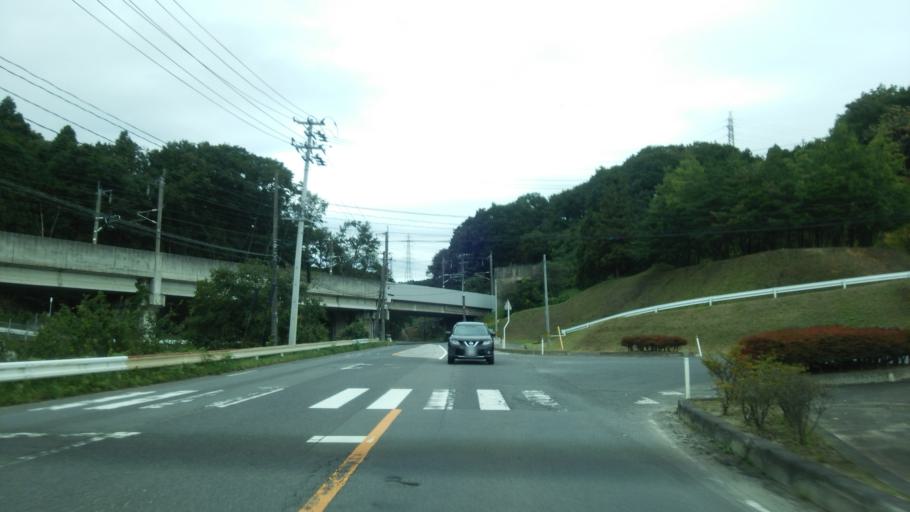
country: JP
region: Fukushima
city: Sukagawa
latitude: 37.1535
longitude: 140.2182
